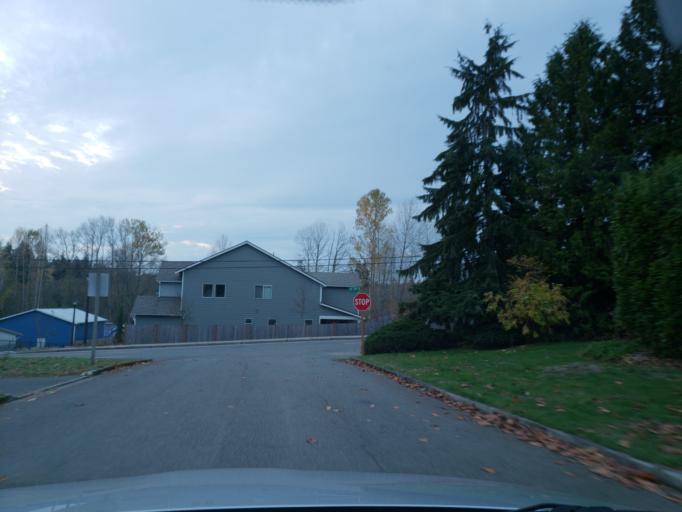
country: US
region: Washington
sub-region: King County
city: Kenmore
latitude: 47.7747
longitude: -122.2404
